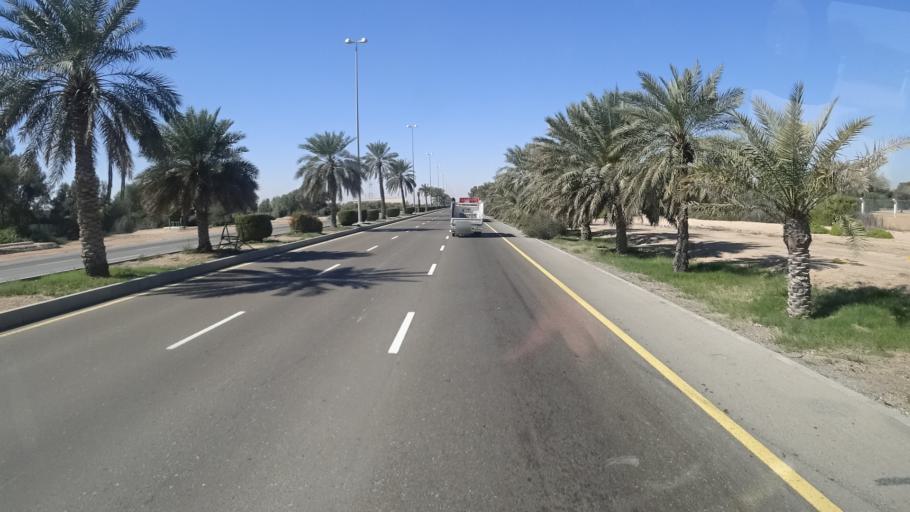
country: AE
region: Abu Dhabi
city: Al Ain
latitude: 24.0825
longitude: 55.6719
